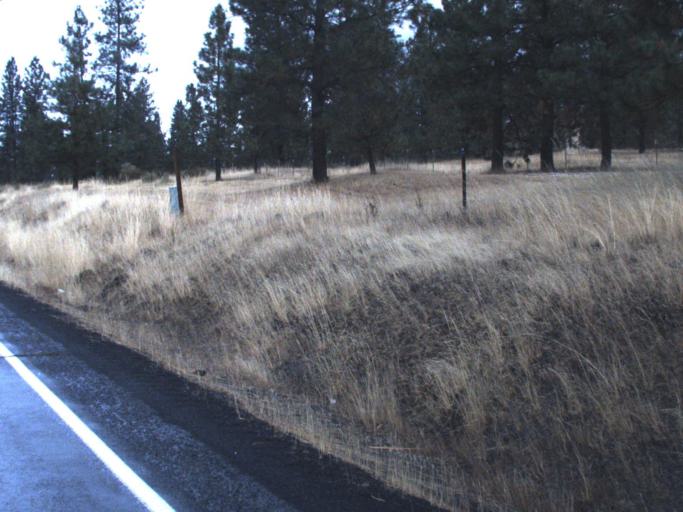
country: US
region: Washington
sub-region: Lincoln County
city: Davenport
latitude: 47.7854
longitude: -117.8893
